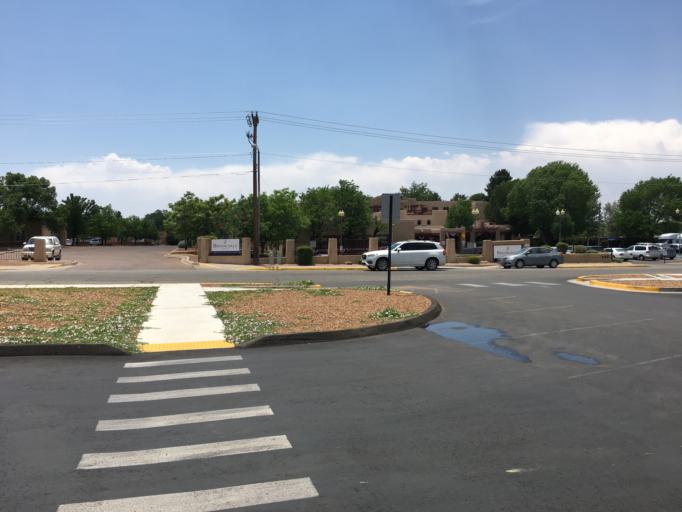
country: US
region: New Mexico
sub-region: Santa Fe County
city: Santa Fe
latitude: 35.6706
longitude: -105.9521
